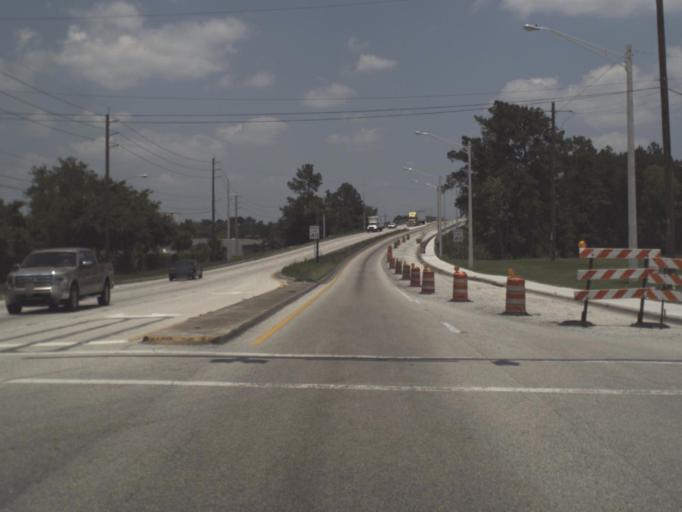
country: US
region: Florida
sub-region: Duval County
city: Jacksonville
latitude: 30.3637
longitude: -81.7303
